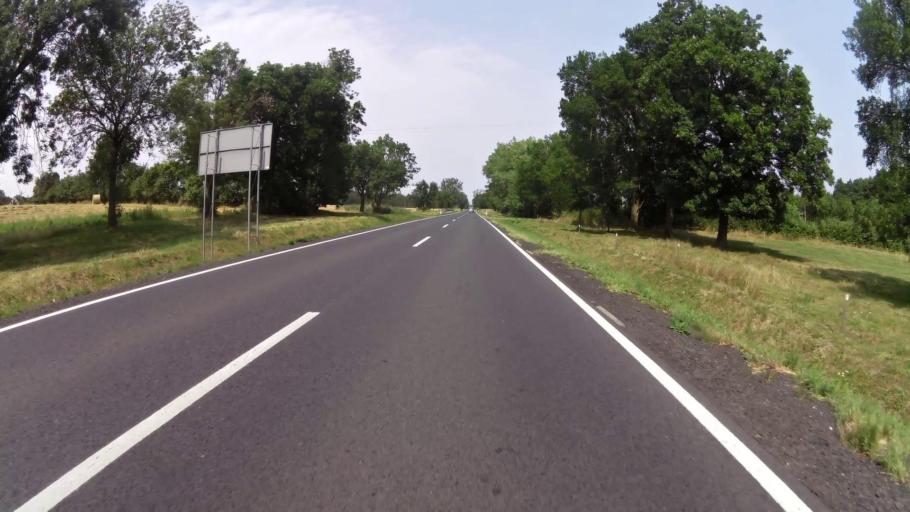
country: PL
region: West Pomeranian Voivodeship
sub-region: Powiat gryfinski
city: Mieszkowice
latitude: 52.8280
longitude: 14.4950
